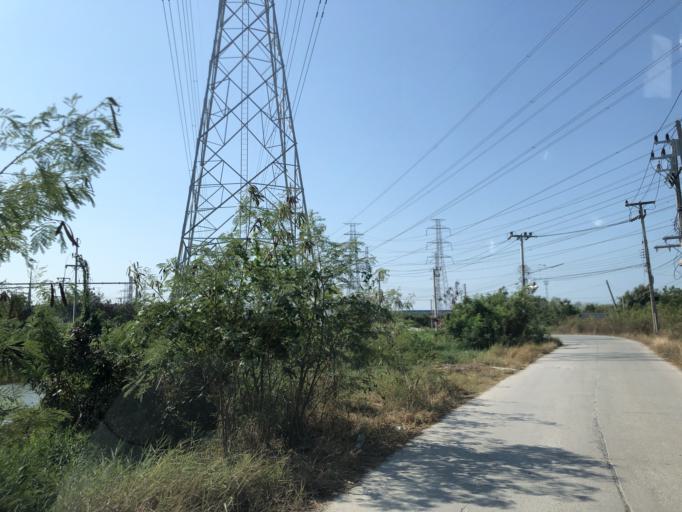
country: TH
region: Chachoengsao
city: Bang Pakong
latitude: 13.5128
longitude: 101.0247
